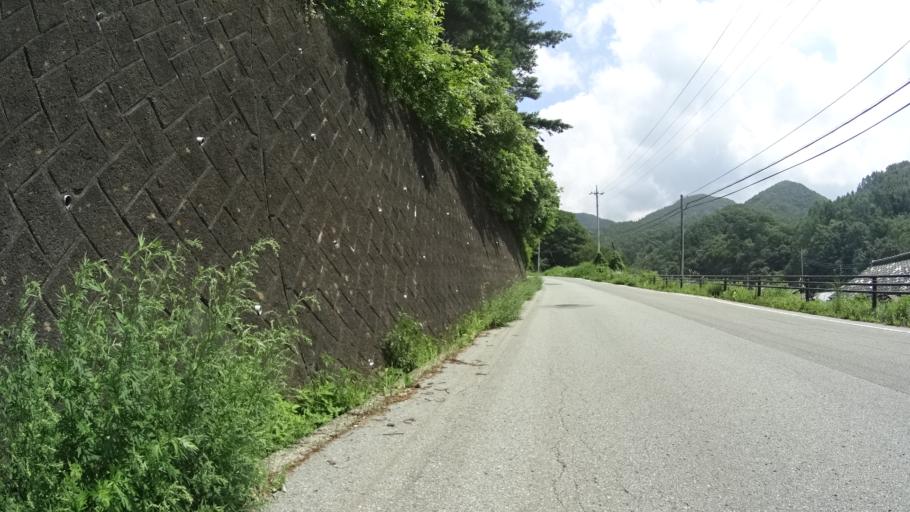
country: JP
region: Yamanashi
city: Nirasaki
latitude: 35.8859
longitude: 138.5260
